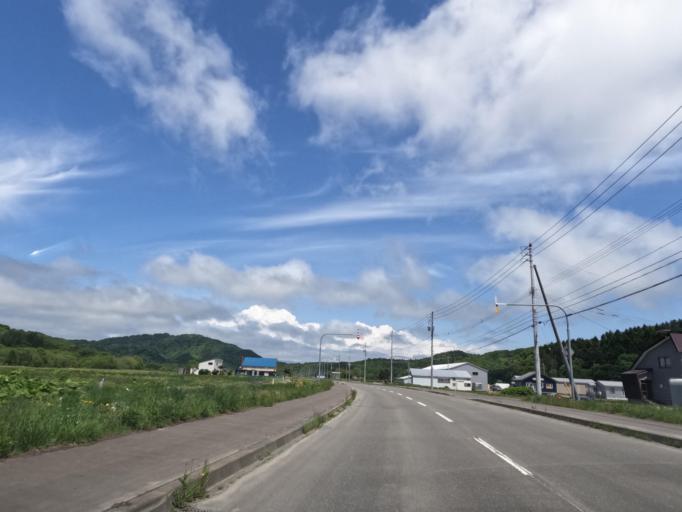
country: JP
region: Hokkaido
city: Tobetsu
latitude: 43.2989
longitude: 141.5469
